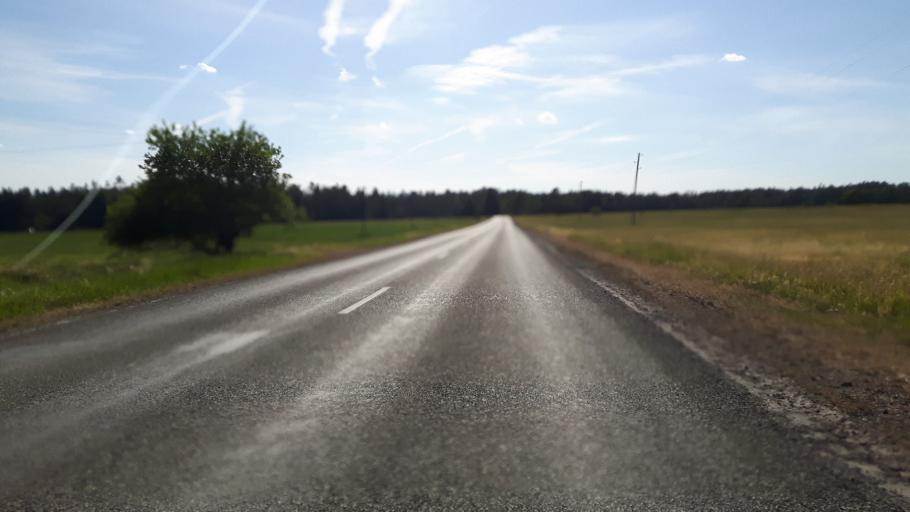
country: LV
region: Talsu Rajons
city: Stende
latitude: 57.0870
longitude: 22.3161
